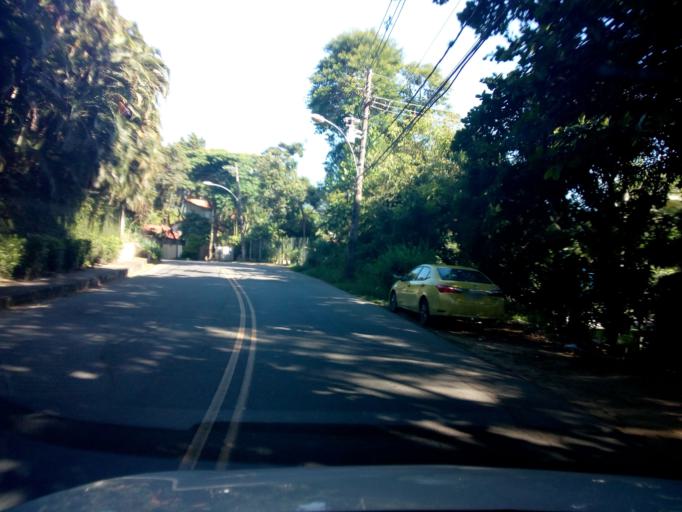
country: BR
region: Rio de Janeiro
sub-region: Nilopolis
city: Nilopolis
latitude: -23.0249
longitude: -43.5011
